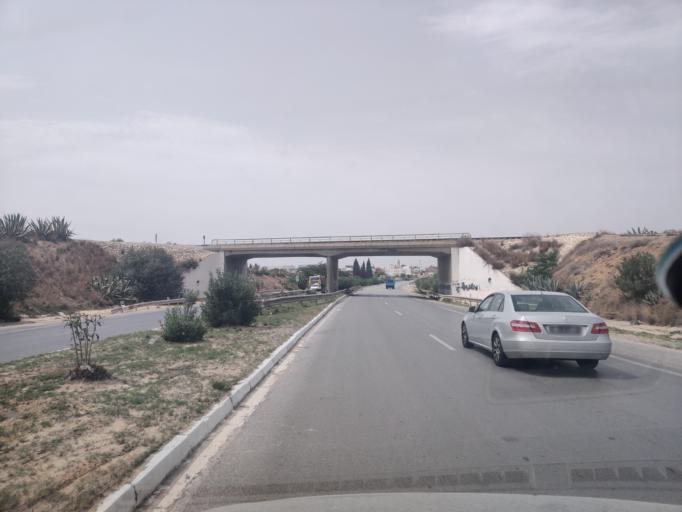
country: TN
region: Susah
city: Akouda
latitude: 35.8336
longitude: 10.5681
